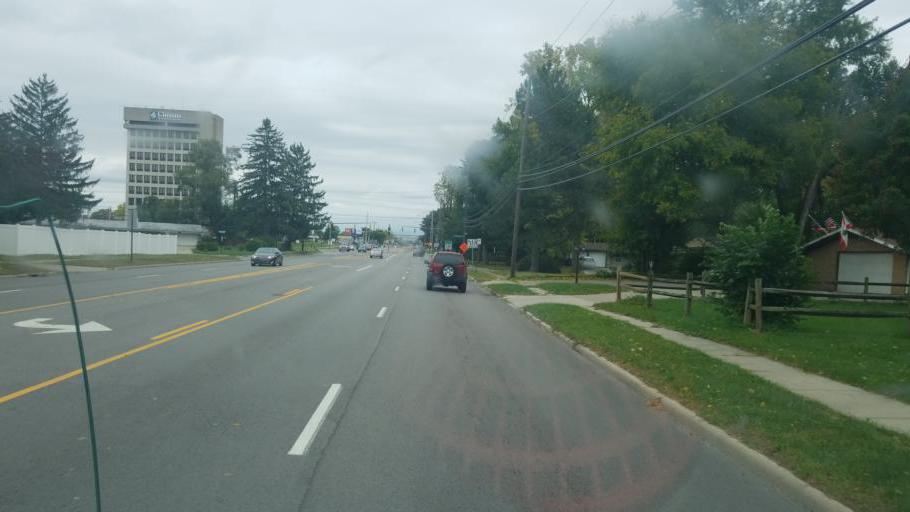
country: US
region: Ohio
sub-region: Lucas County
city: Ottawa Hills
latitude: 41.6772
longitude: -83.6313
